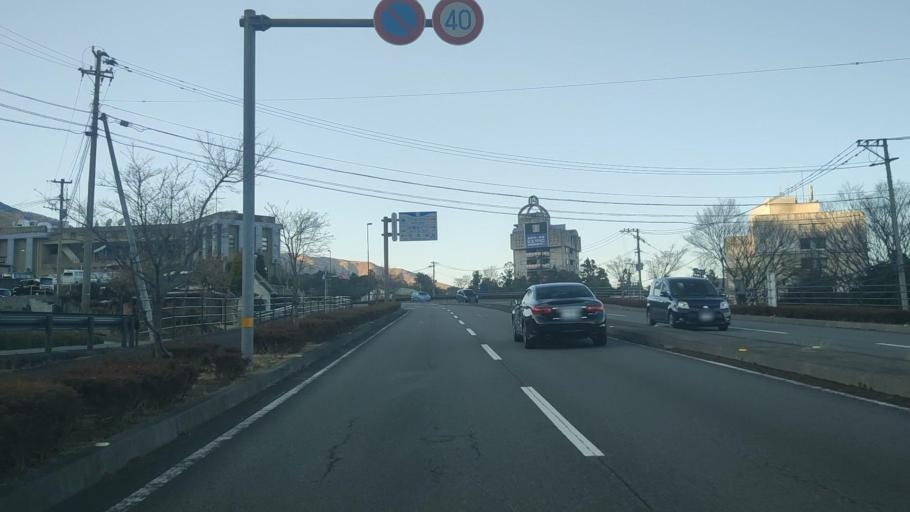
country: JP
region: Oita
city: Beppu
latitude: 33.2897
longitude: 131.4609
